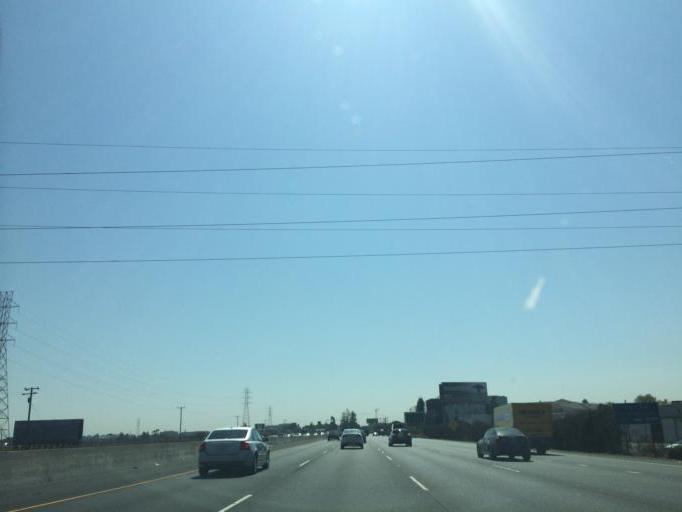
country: US
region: California
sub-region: San Mateo County
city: Redwood City
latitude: 37.5017
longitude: -122.2424
